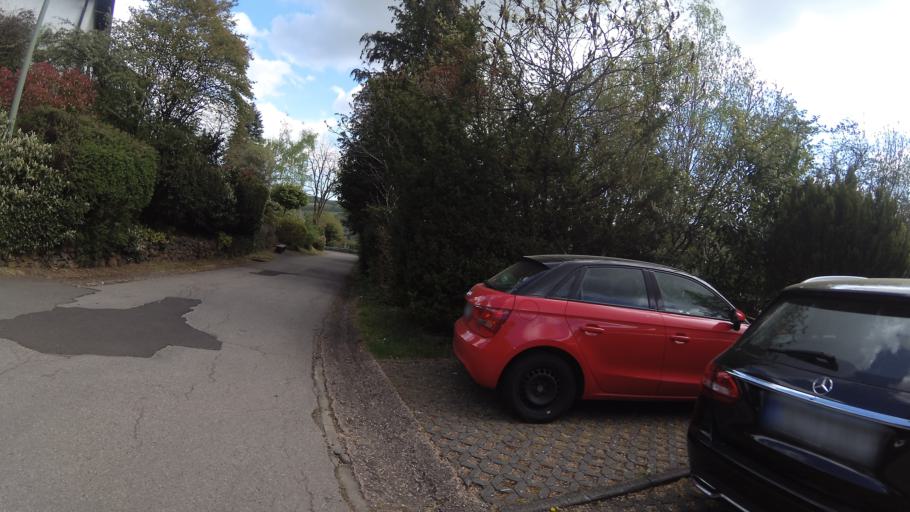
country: DE
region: Saarland
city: Wadern
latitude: 49.4955
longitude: 6.8617
